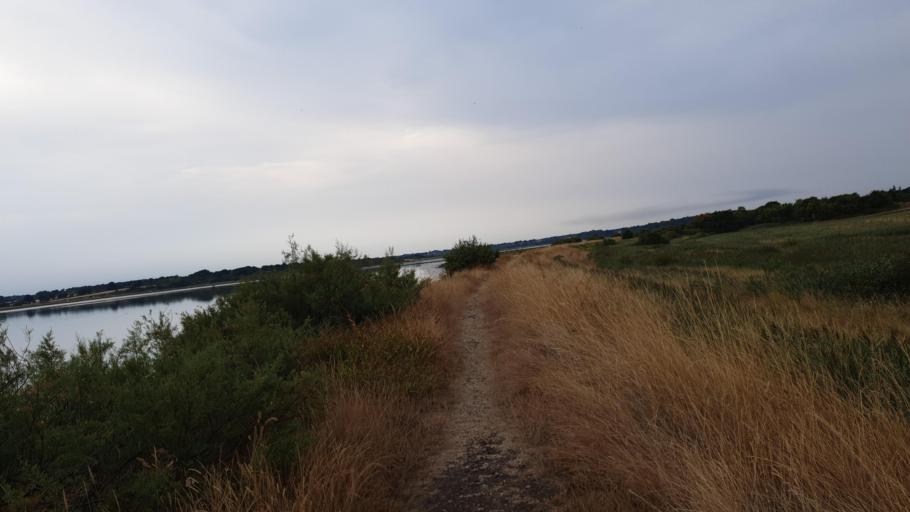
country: GB
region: England
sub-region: Essex
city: Alresford
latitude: 51.8249
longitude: 0.9865
